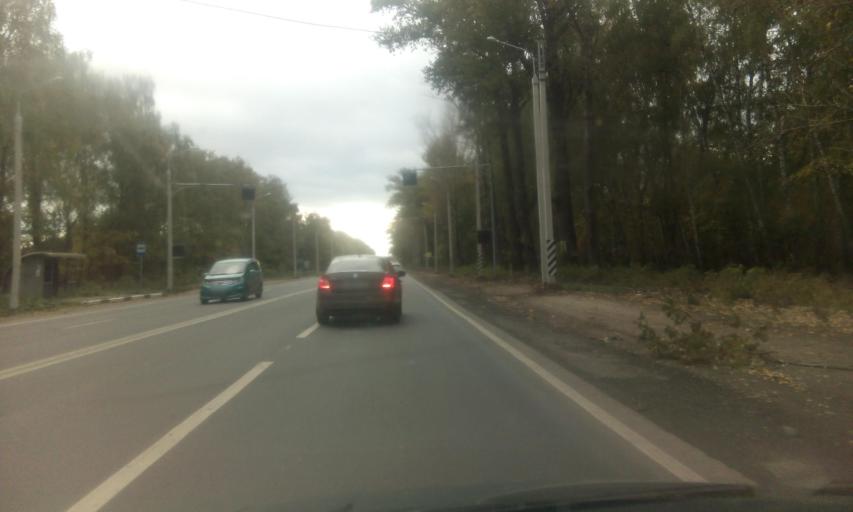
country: RU
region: Tula
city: Kamenetskiy
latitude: 53.9987
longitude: 38.2277
